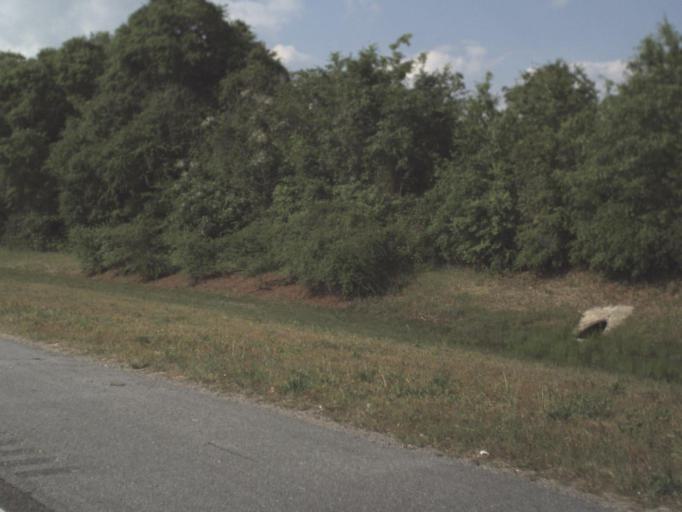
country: US
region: Florida
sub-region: Escambia County
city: Brent
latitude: 30.4621
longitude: -87.2254
